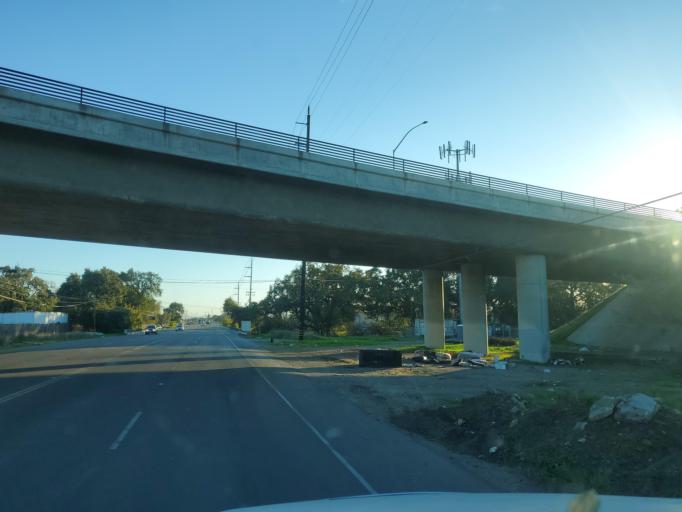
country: US
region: California
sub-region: San Joaquin County
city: French Camp
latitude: 37.8956
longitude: -121.2759
